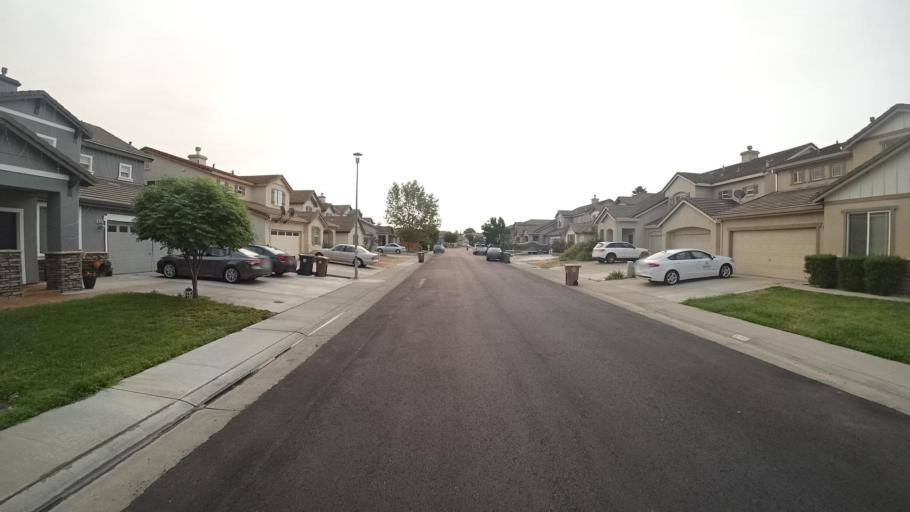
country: US
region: California
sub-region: Sacramento County
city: Laguna
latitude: 38.4346
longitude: -121.4042
